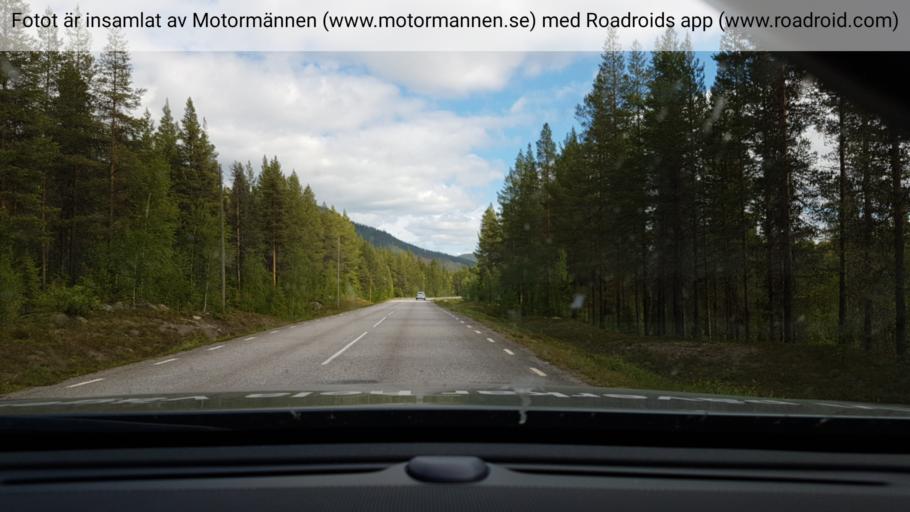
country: SE
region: Vaesterbotten
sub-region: Sorsele Kommun
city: Sorsele
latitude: 65.6786
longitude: 17.3633
